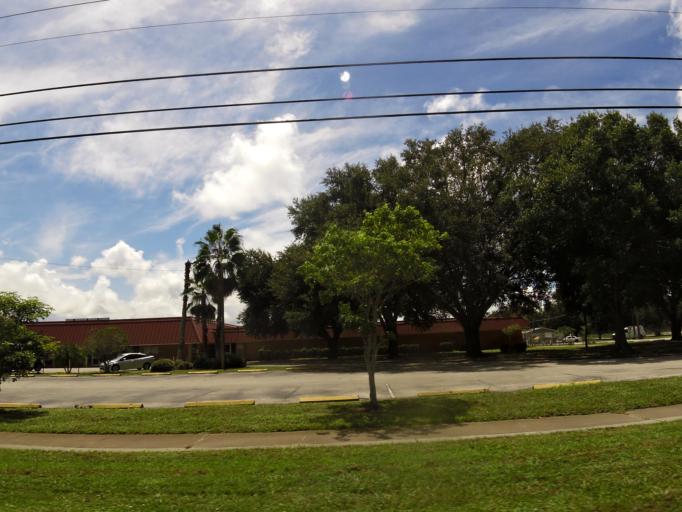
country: US
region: Florida
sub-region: Brevard County
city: Mims
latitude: 28.6371
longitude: -80.8498
